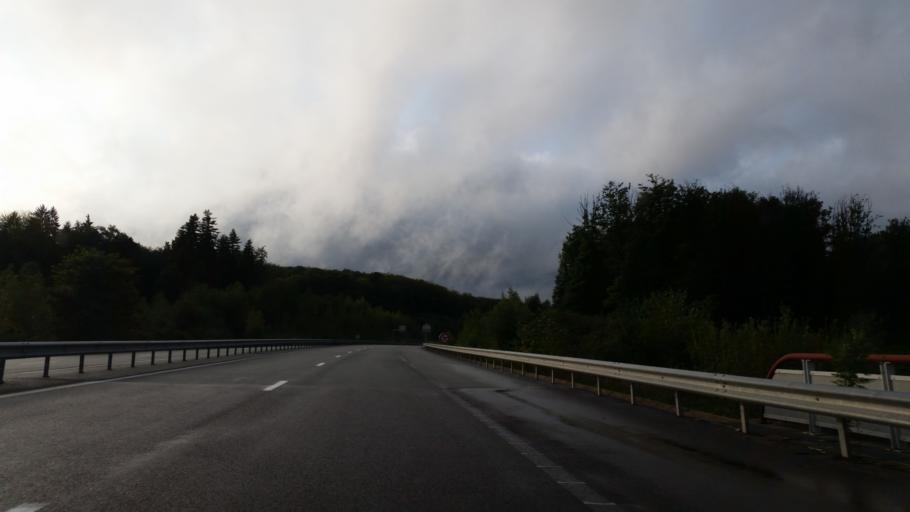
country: FR
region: Franche-Comte
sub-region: Departement de la Haute-Saone
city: Luxeuil-les-Bains
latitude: 47.8489
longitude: 6.3876
